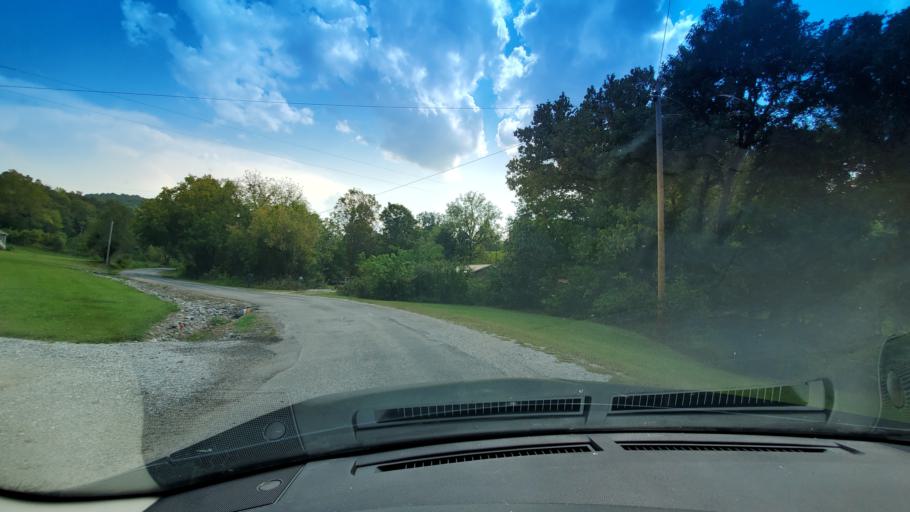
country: US
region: Tennessee
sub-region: Smith County
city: South Carthage
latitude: 36.2371
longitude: -85.9781
